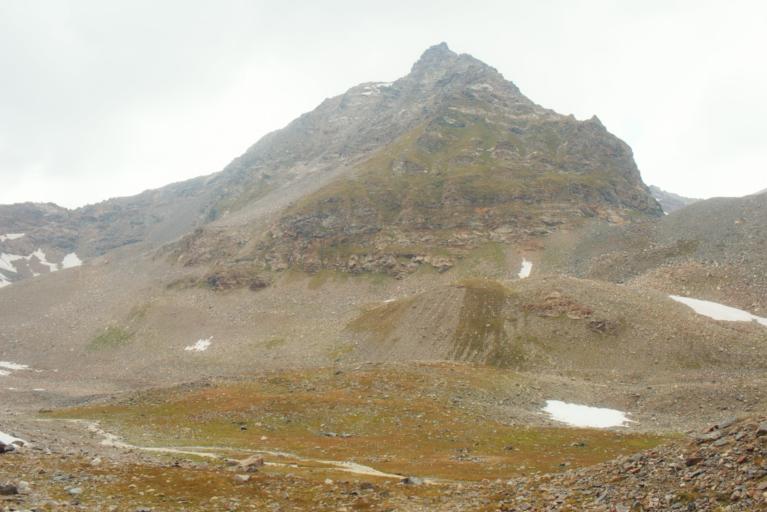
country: RU
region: Karachayevo-Cherkesiya
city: Nizhniy Arkhyz
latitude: 43.4289
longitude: 41.2546
